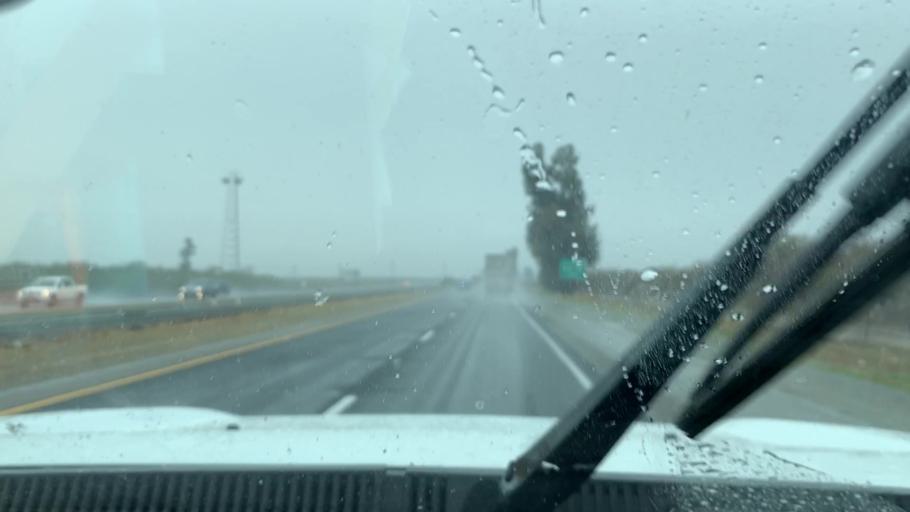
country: US
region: California
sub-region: Tulare County
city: Earlimart
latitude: 35.8597
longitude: -119.2684
